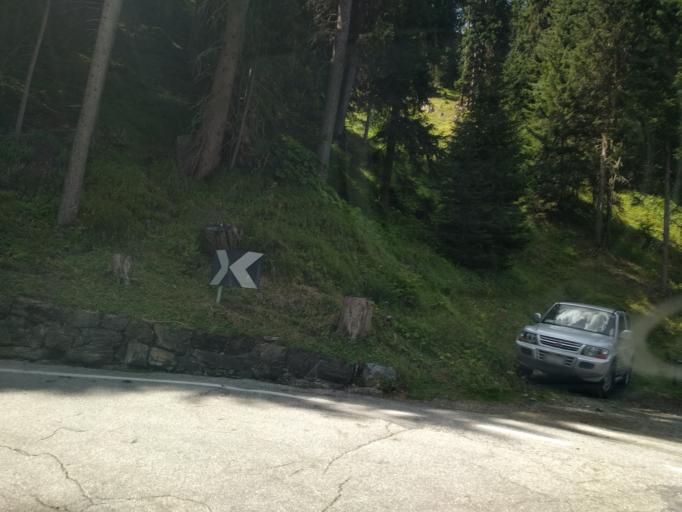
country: IT
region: Trentino-Alto Adige
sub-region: Bolzano
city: Stelvio
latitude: 46.5451
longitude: 10.5050
